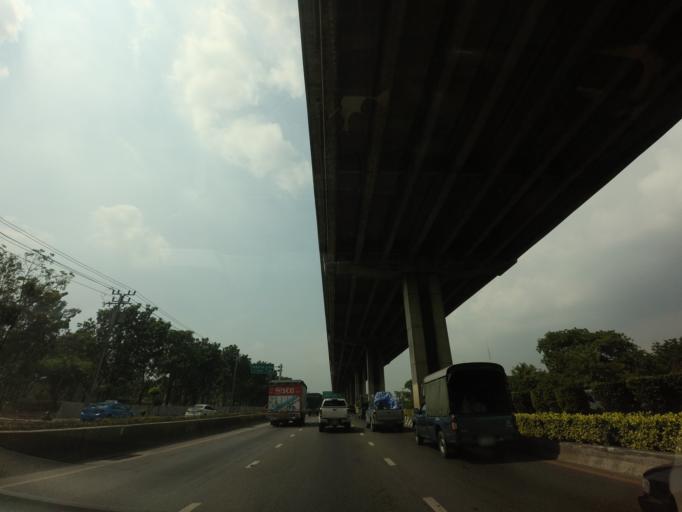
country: TH
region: Bangkok
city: Thawi Watthana
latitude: 13.7844
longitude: 100.3930
